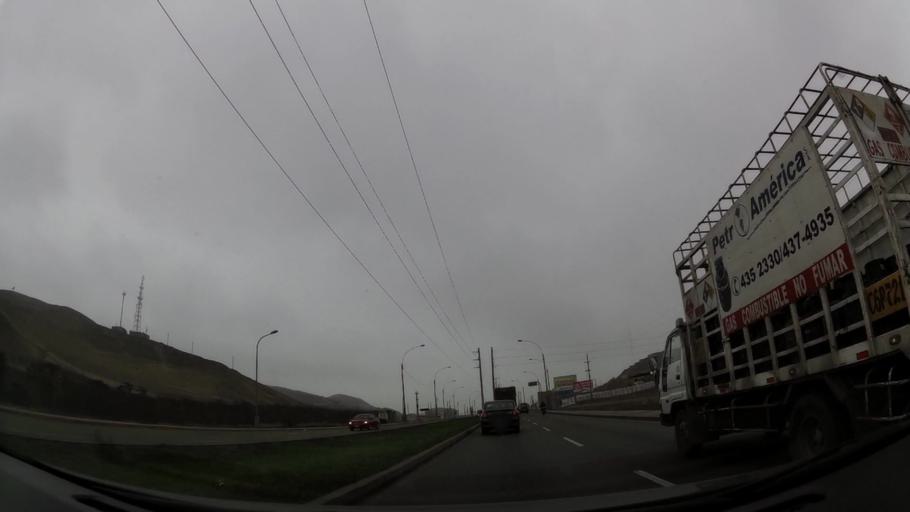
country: PE
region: Lima
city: Ventanilla
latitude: -11.9052
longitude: -77.1285
